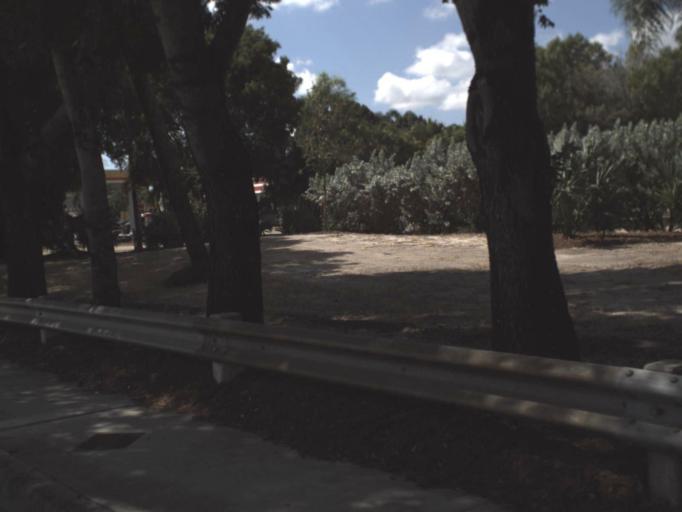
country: US
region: Florida
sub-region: Lee County
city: Fort Myers
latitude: 26.6113
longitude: -81.8721
